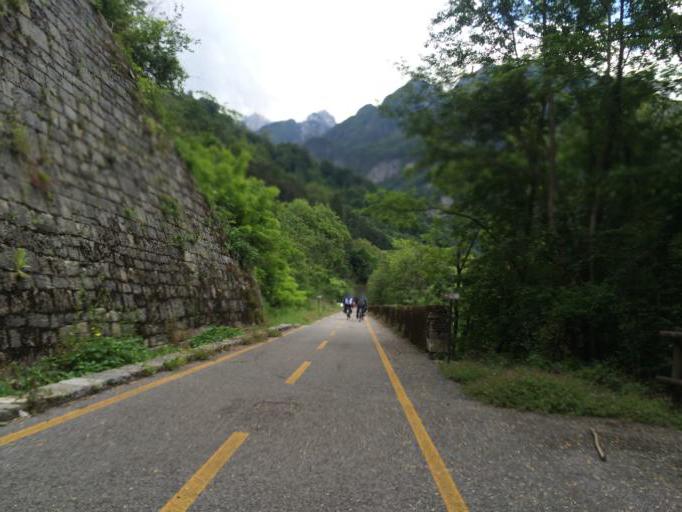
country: IT
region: Friuli Venezia Giulia
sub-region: Provincia di Udine
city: Dogna
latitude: 46.4547
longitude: 13.3140
